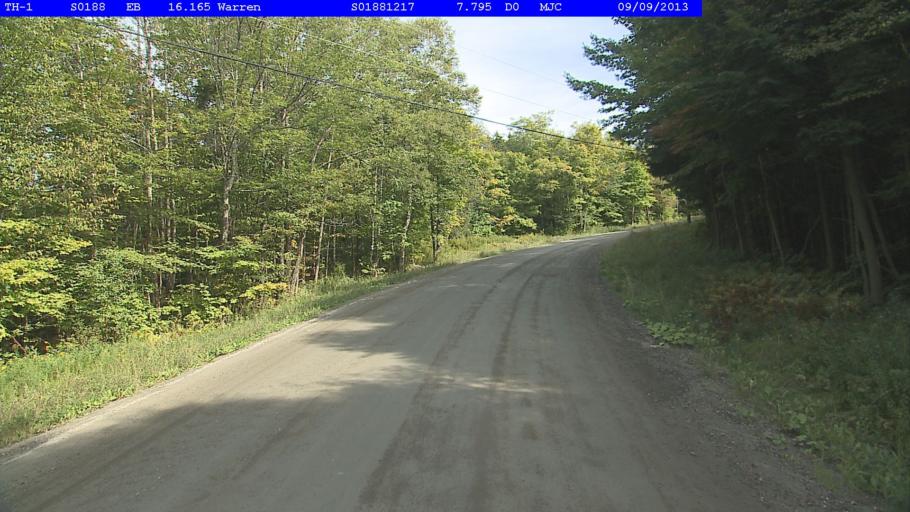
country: US
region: Vermont
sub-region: Washington County
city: Northfield
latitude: 44.1088
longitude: -72.7999
